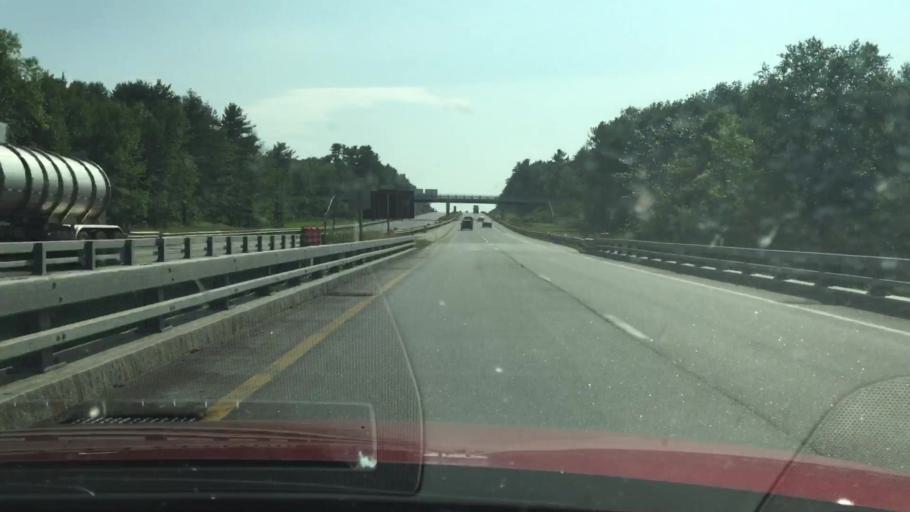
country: US
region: Maine
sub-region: Kennebec County
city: Gardiner
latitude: 44.1790
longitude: -69.8605
